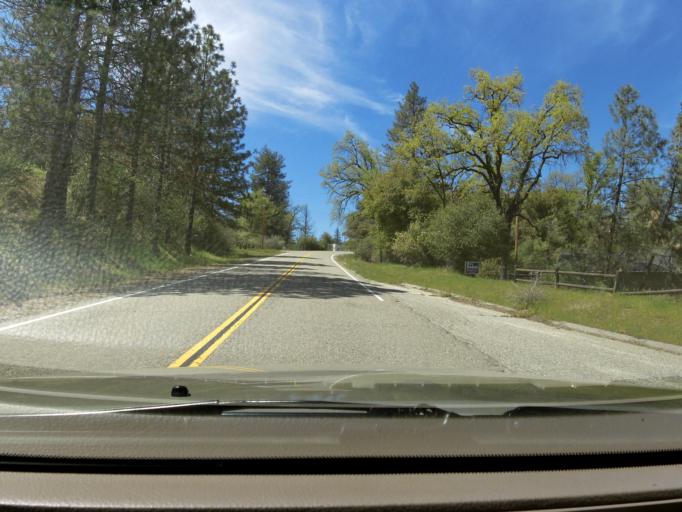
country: US
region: California
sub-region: Madera County
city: Oakhurst
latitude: 37.2490
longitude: -119.5646
